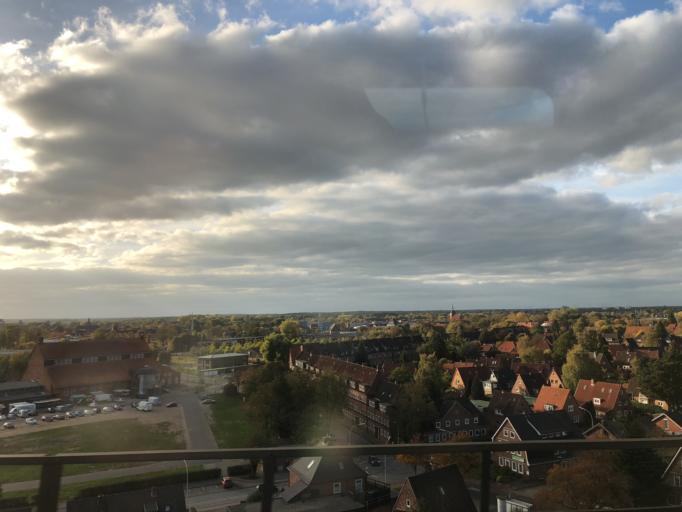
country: DE
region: Schleswig-Holstein
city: Rendsburg
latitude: 54.3008
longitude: 9.6799
